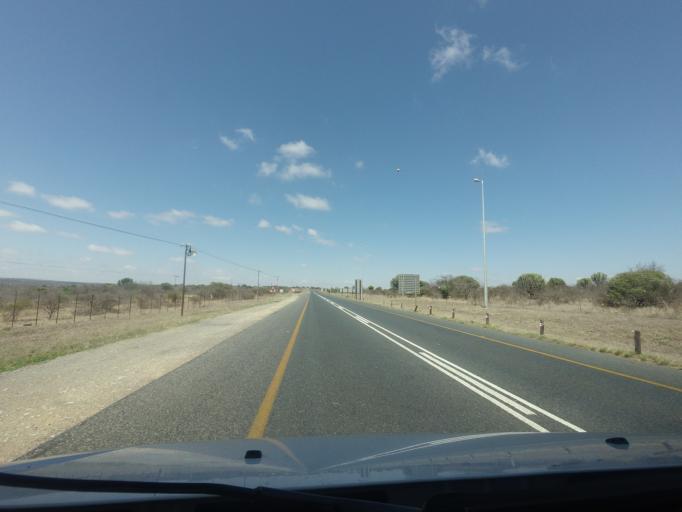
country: ZA
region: Limpopo
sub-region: Vhembe District Municipality
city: Louis Trichardt
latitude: -23.3689
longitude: 29.7734
